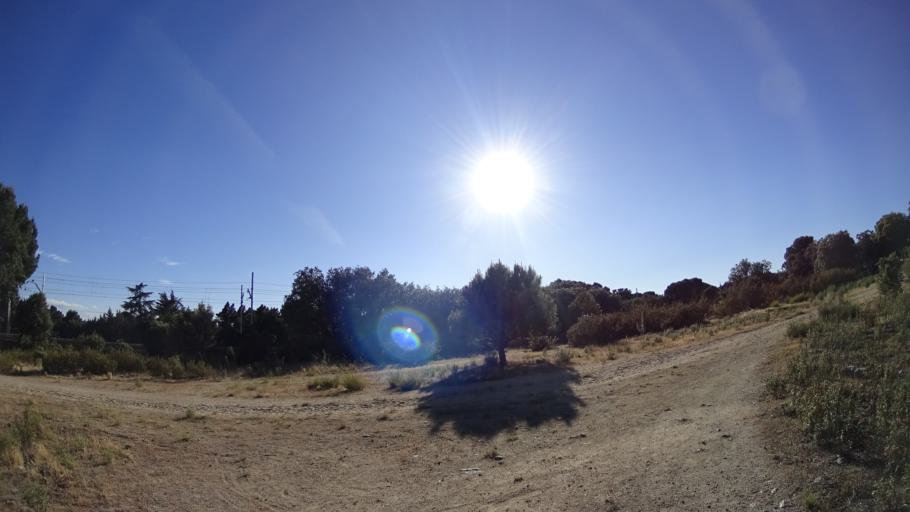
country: ES
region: Madrid
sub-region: Provincia de Madrid
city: Torrelodones
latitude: 40.5867
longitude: -3.9627
